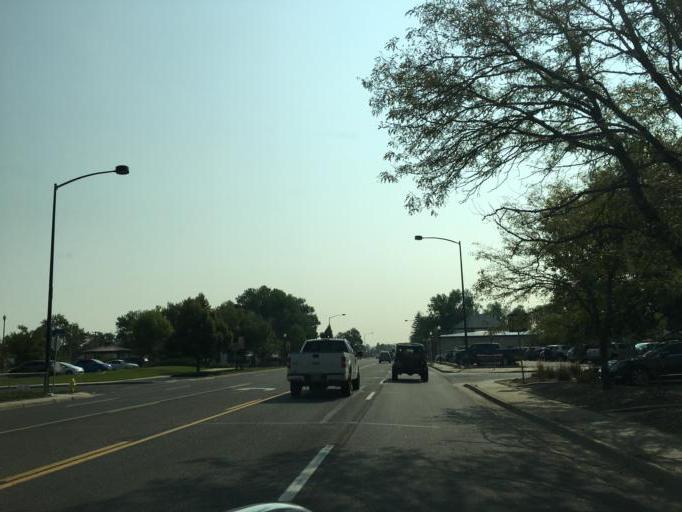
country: US
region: Colorado
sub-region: Adams County
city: Brighton
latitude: 39.9868
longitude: -104.8175
